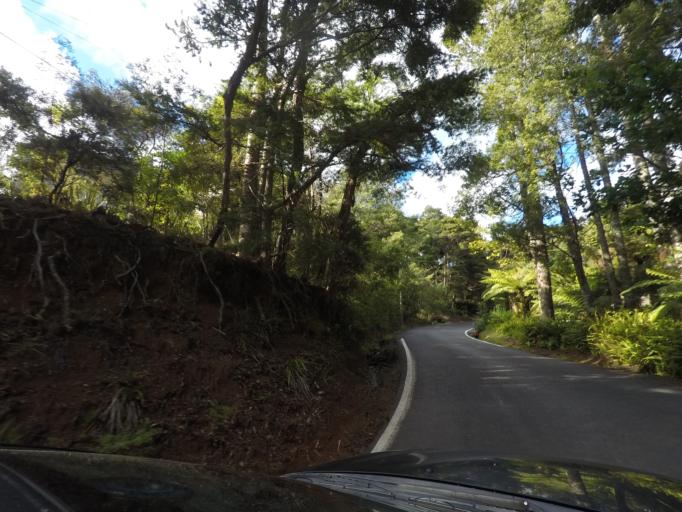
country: NZ
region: Auckland
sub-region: Auckland
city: Titirangi
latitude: -37.0164
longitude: 174.5538
